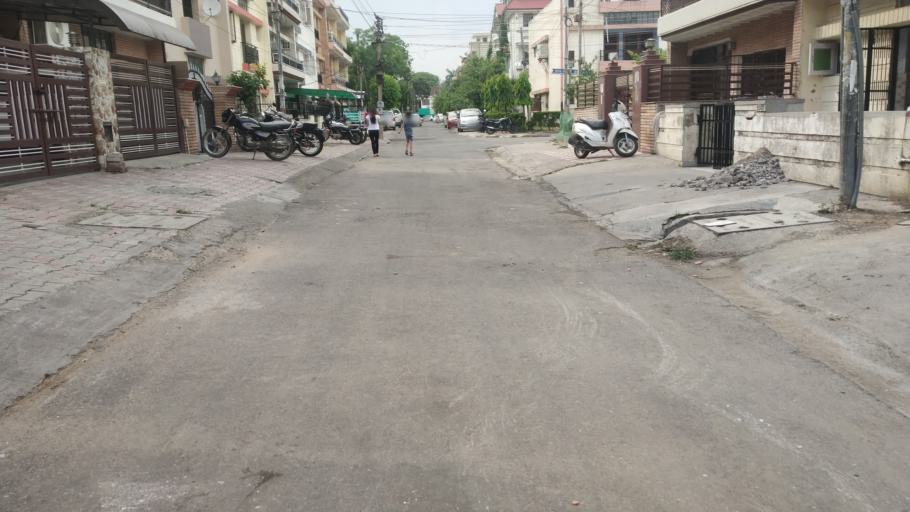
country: IN
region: Punjab
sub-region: Ajitgarh
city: Mohali
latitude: 30.7059
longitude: 76.7175
